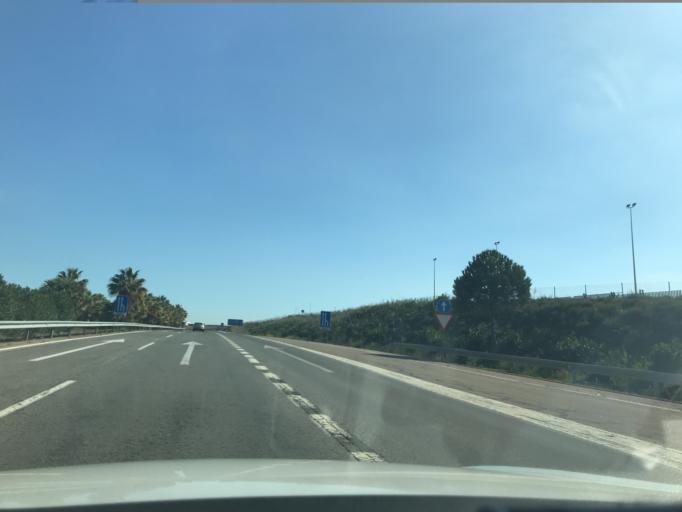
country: ES
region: Andalusia
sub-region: Provincia de Sevilla
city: Ecija
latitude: 37.5760
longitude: -4.9997
